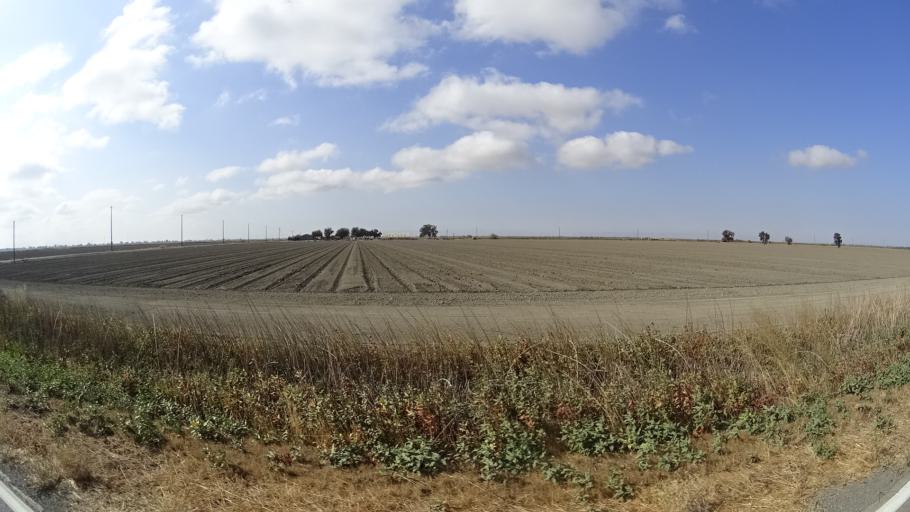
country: US
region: California
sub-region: Yolo County
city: Woodland
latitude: 38.8277
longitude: -121.7477
